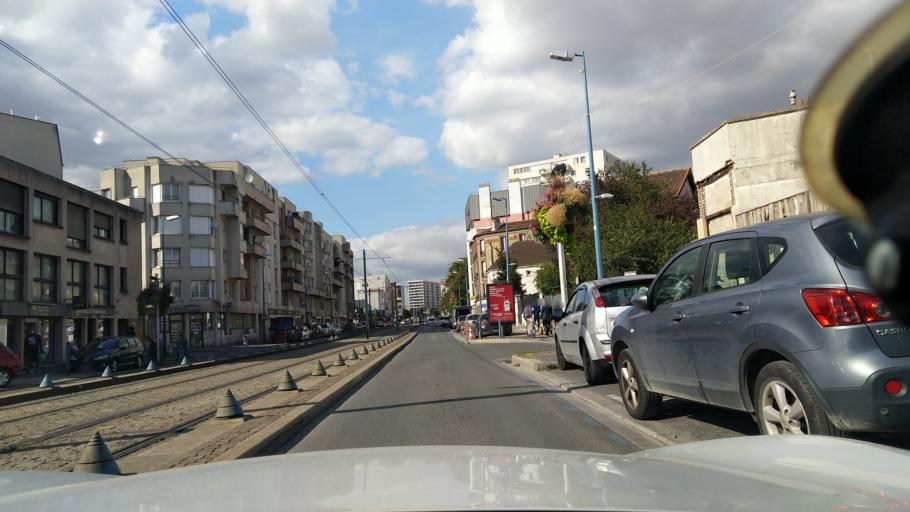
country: FR
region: Ile-de-France
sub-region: Departement de Seine-Saint-Denis
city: Bobigny
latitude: 48.9079
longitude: 2.4383
